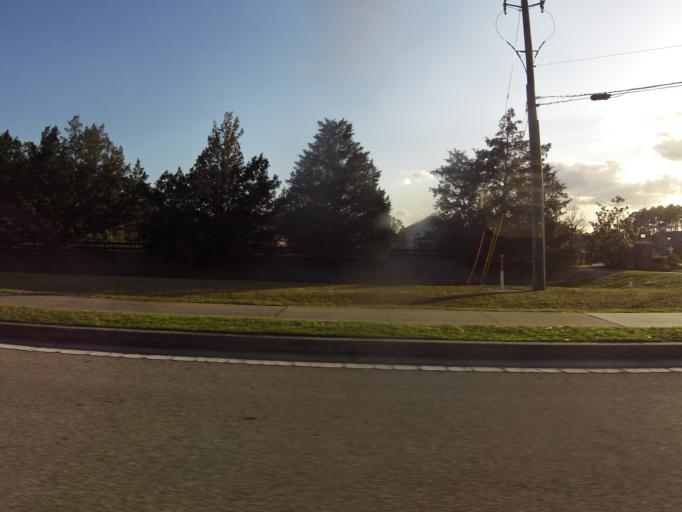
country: US
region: Florida
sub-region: Saint Johns County
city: Fruit Cove
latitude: 30.0730
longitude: -81.5159
